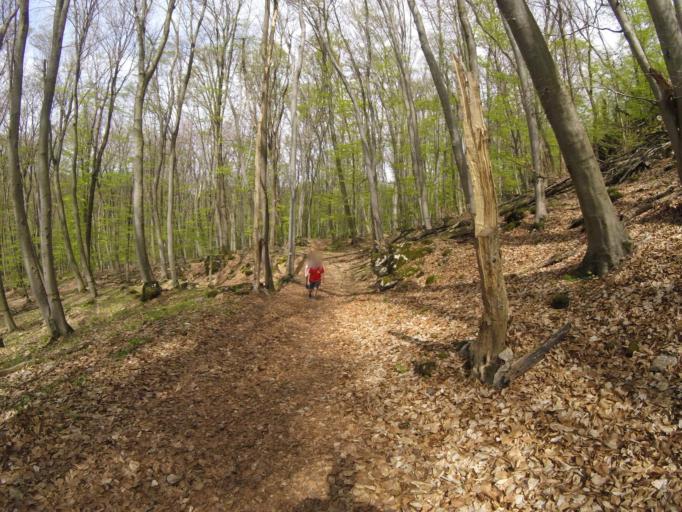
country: HU
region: Borsod-Abauj-Zemplen
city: Szendro
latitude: 48.5434
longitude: 20.6604
